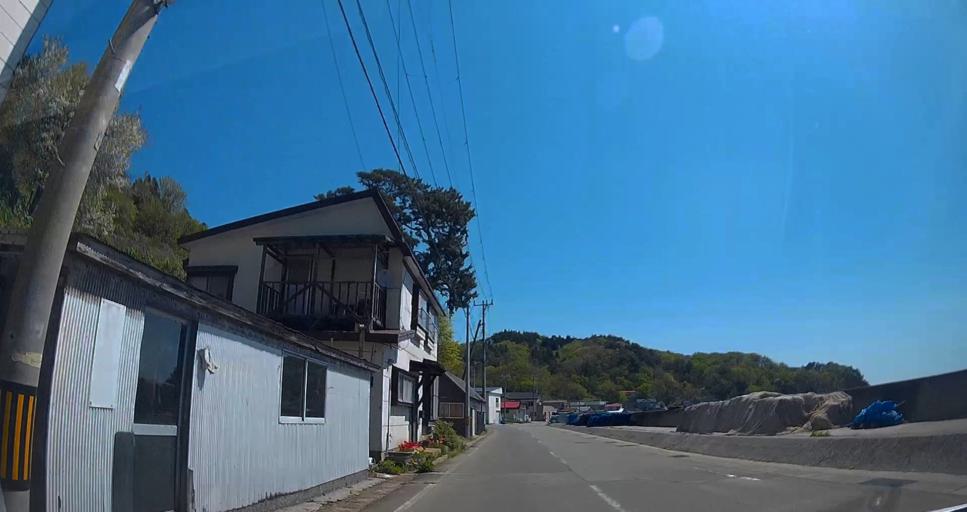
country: JP
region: Aomori
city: Aomori Shi
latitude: 41.1297
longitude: 140.8048
